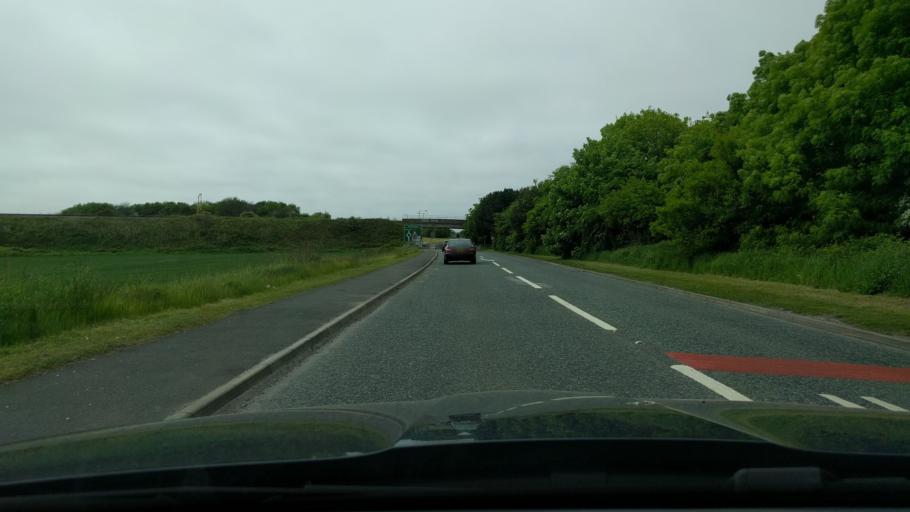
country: GB
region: England
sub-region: Northumberland
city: Newbiggin-by-the-Sea
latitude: 55.1900
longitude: -1.5375
